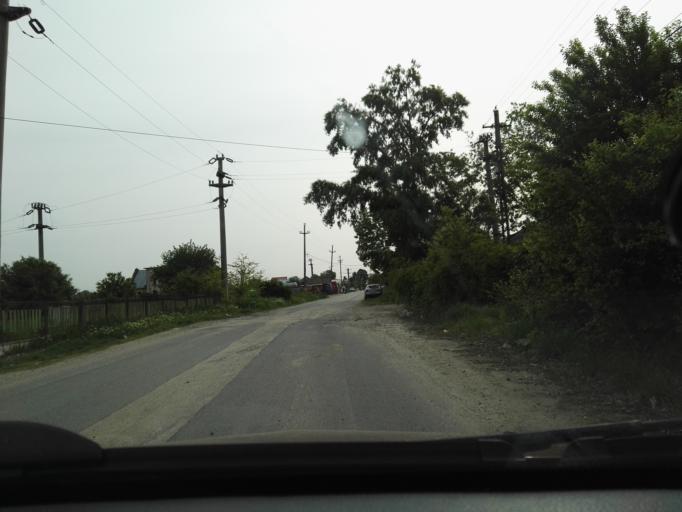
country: RO
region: Giurgiu
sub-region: Comuna Mihailesti
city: Mihailesti
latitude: 44.3425
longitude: 25.8814
